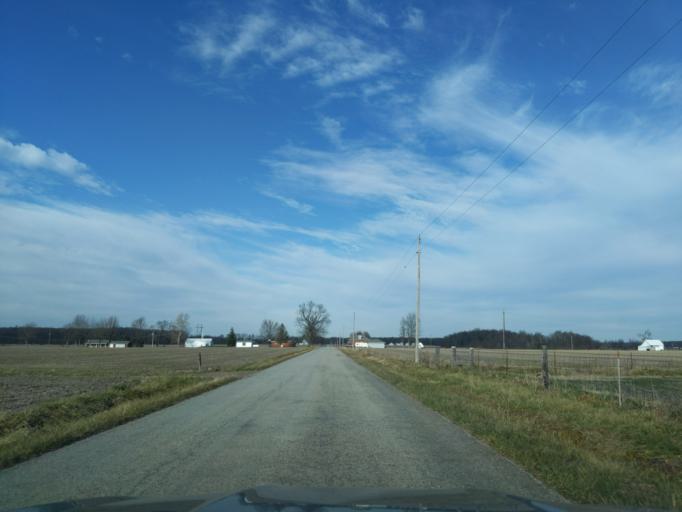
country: US
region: Indiana
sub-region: Decatur County
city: Greensburg
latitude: 39.2487
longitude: -85.4193
